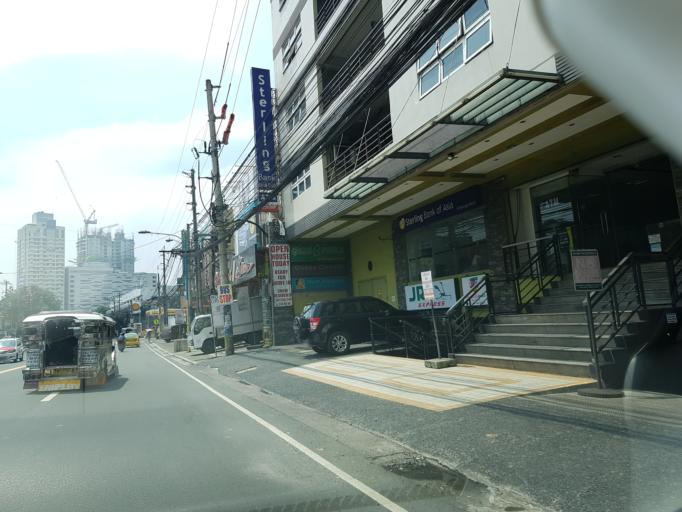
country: PH
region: Metro Manila
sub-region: Mandaluyong
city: Mandaluyong City
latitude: 14.5887
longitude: 121.0430
